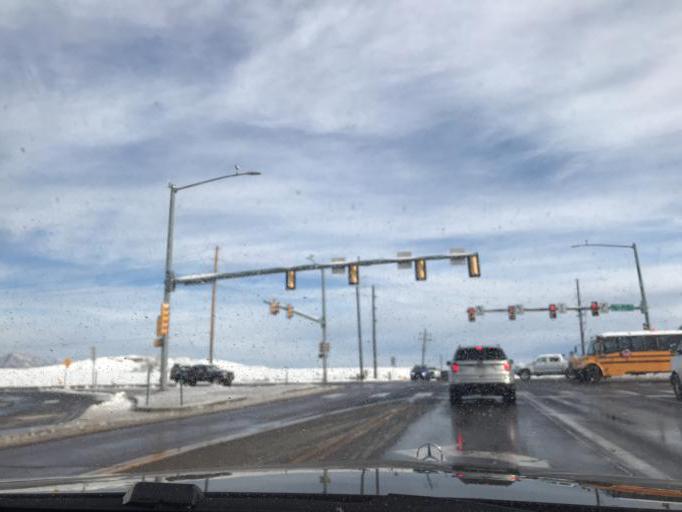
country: US
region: Colorado
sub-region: Jefferson County
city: Arvada
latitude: 39.8501
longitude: -105.1653
